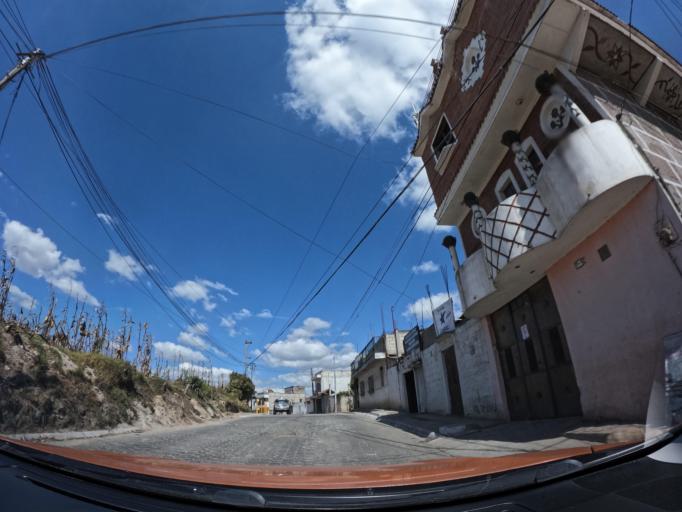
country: GT
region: Chimaltenango
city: Patzun
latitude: 14.6707
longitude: -91.0100
